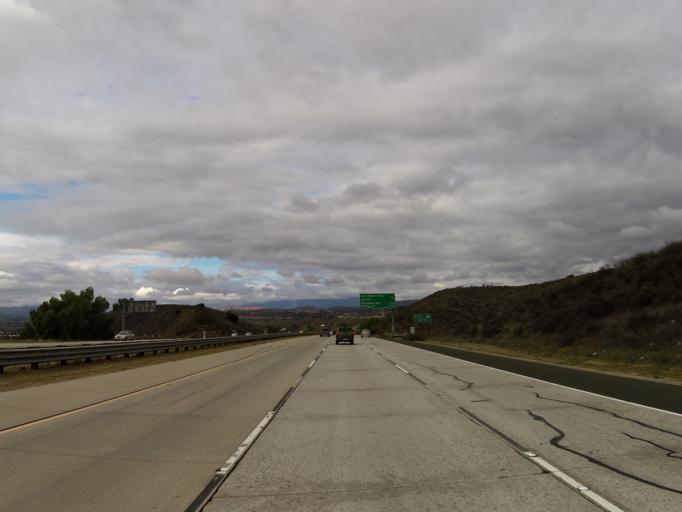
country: US
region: California
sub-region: Ventura County
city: Moorpark
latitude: 34.2742
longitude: -118.8570
